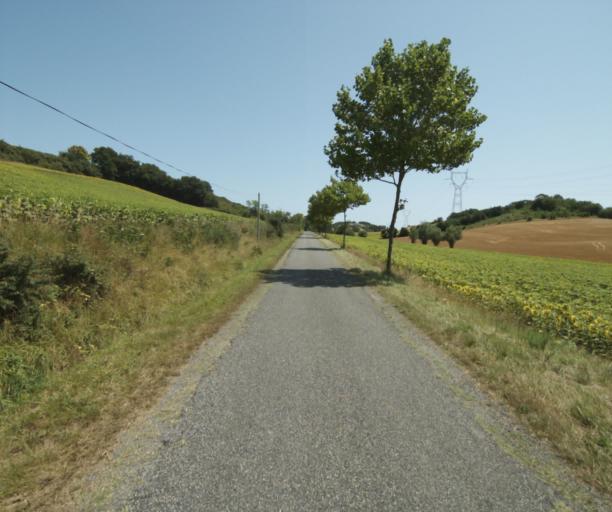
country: FR
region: Midi-Pyrenees
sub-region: Departement de la Haute-Garonne
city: Saint-Felix-Lauragais
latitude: 43.4472
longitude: 1.8453
